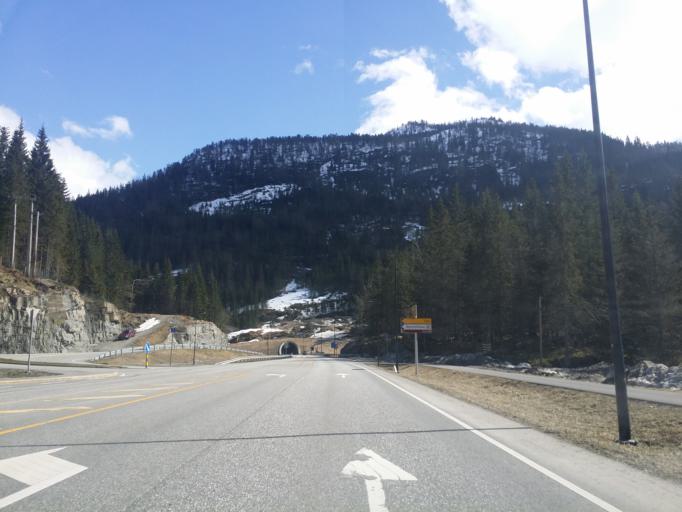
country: NO
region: Hordaland
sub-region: Granvin
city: Granvin
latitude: 60.5867
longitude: 6.6091
